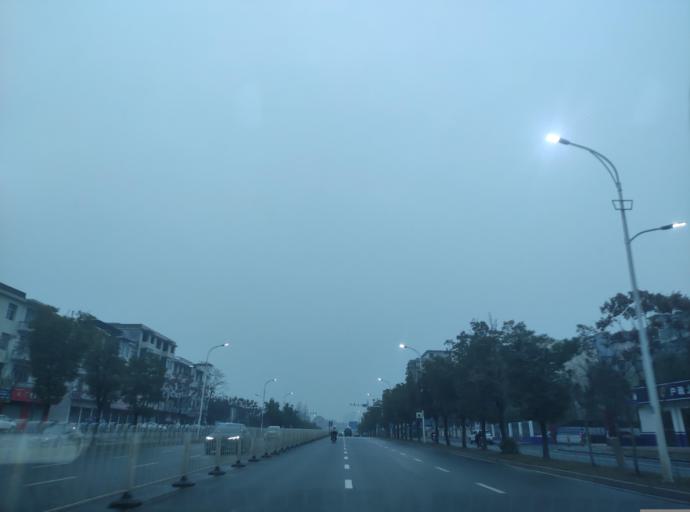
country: CN
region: Jiangxi Sheng
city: Pingxiang
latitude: 27.6686
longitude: 113.8685
